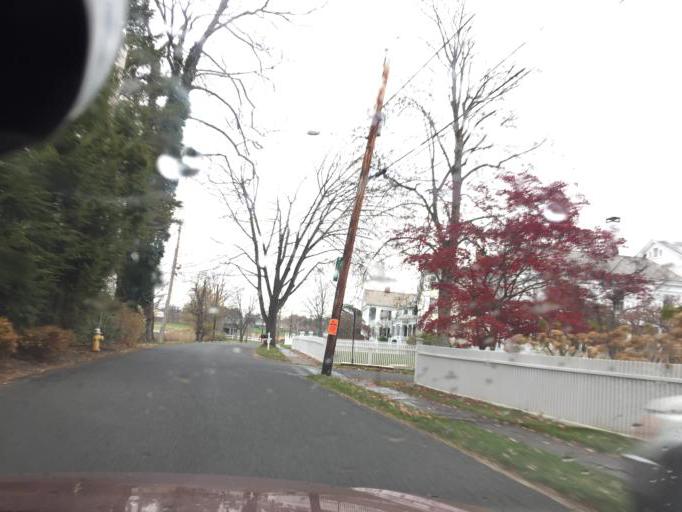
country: US
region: Connecticut
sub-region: Fairfield County
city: Southport
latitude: 41.1324
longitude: -73.2871
